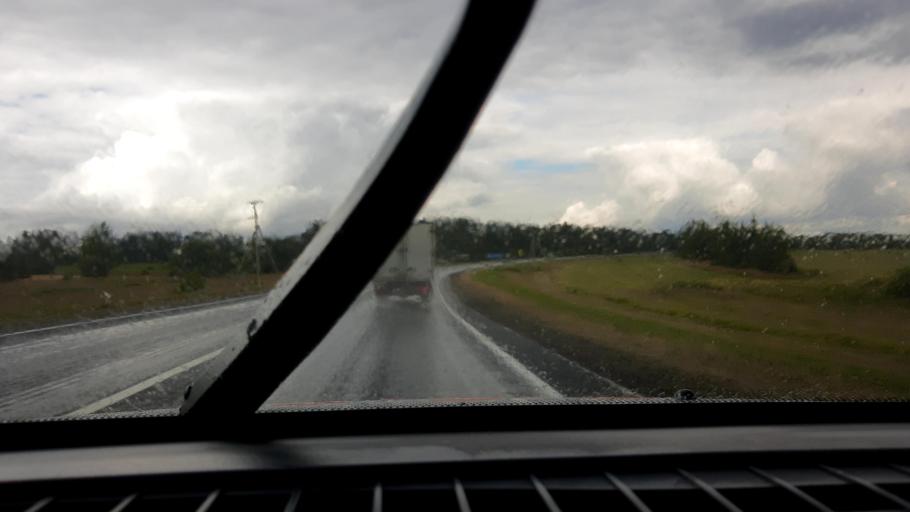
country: RU
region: Nizjnij Novgorod
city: Bol'shoye Murashkino
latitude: 55.9108
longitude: 44.6984
